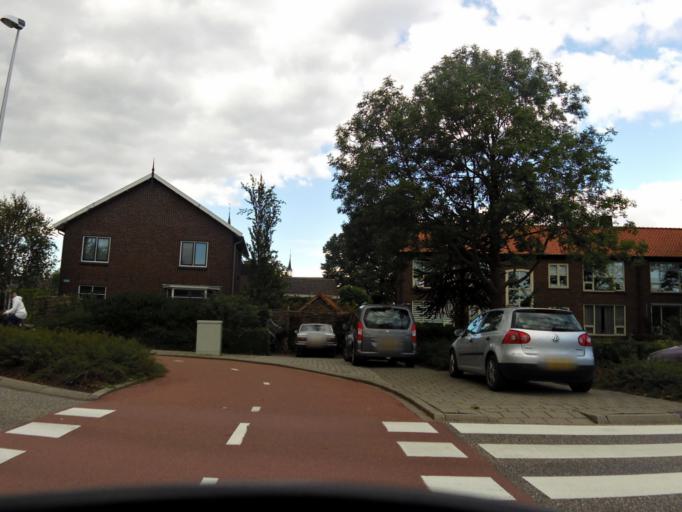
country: NL
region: South Holland
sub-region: Gemeente Alphen aan den Rijn
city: Alphen aan den Rijn
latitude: 52.1308
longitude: 4.5921
